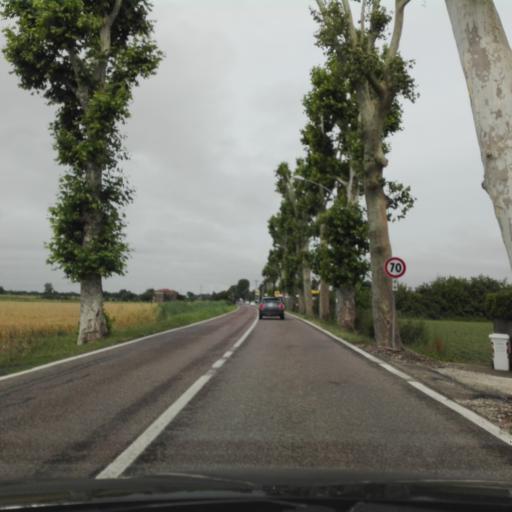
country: IT
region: Veneto
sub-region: Provincia di Rovigo
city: Rovigo
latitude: 45.0787
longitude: 11.7584
